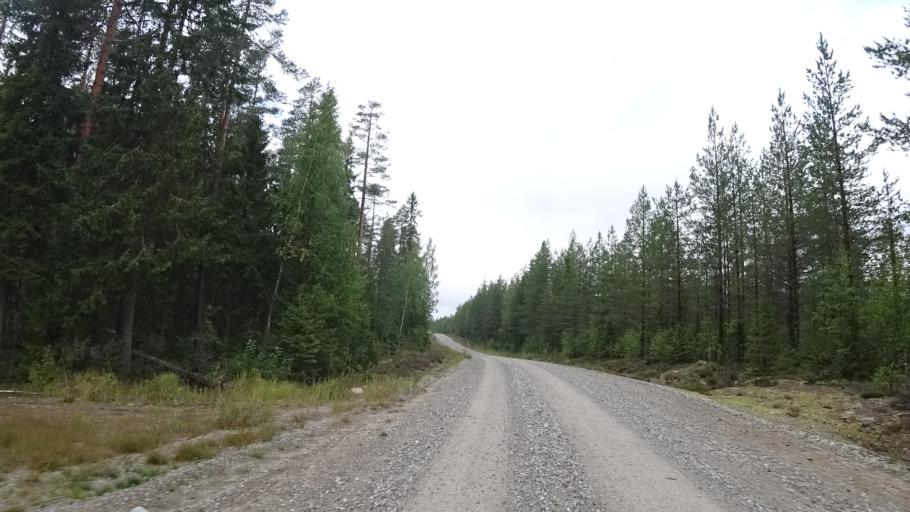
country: FI
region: North Karelia
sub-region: Pielisen Karjala
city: Lieksa
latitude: 63.4646
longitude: 30.2997
